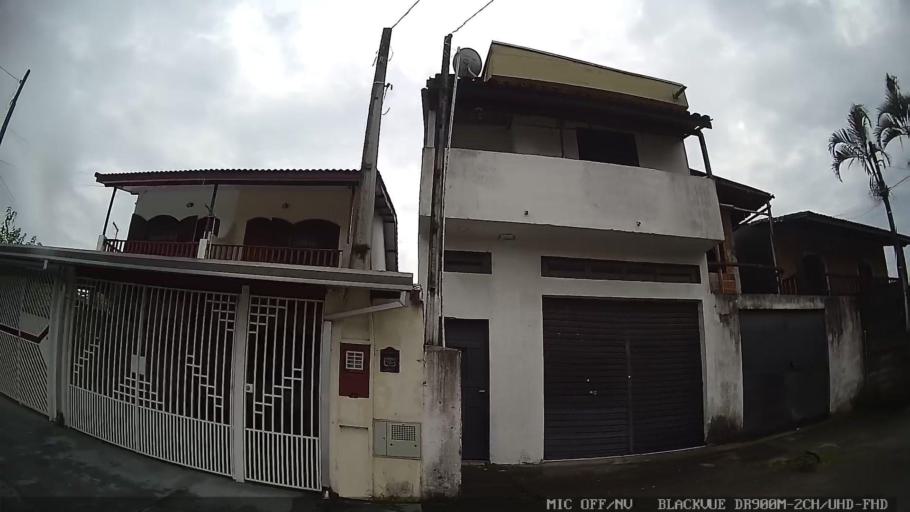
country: BR
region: Sao Paulo
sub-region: Sao Sebastiao
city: Sao Sebastiao
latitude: -23.6948
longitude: -45.4442
